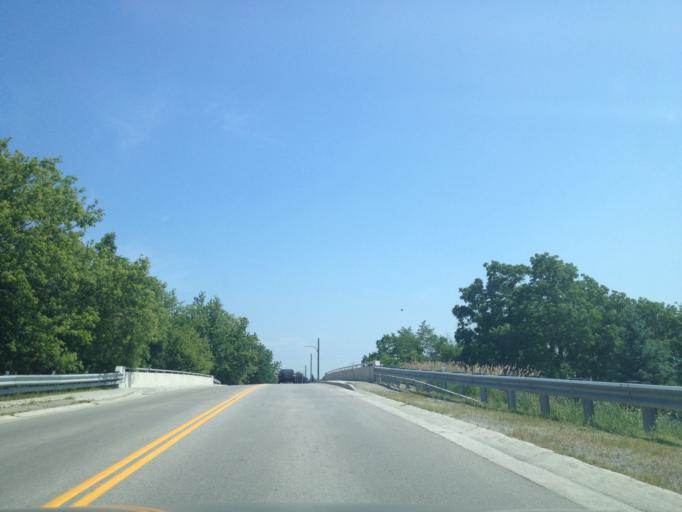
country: CA
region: Ontario
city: Huron East
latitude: 43.4640
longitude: -81.2040
